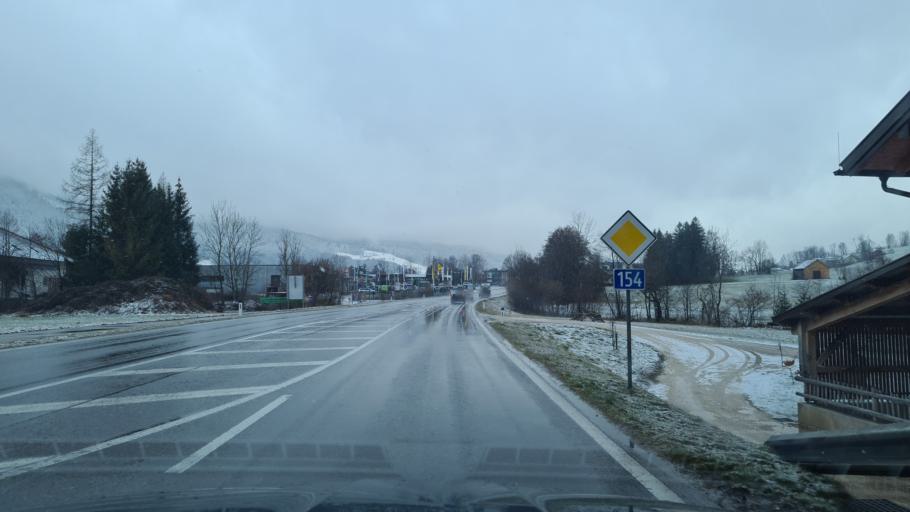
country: AT
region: Upper Austria
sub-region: Politischer Bezirk Vocklabruck
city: Mondsee
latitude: 47.8668
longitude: 13.3280
